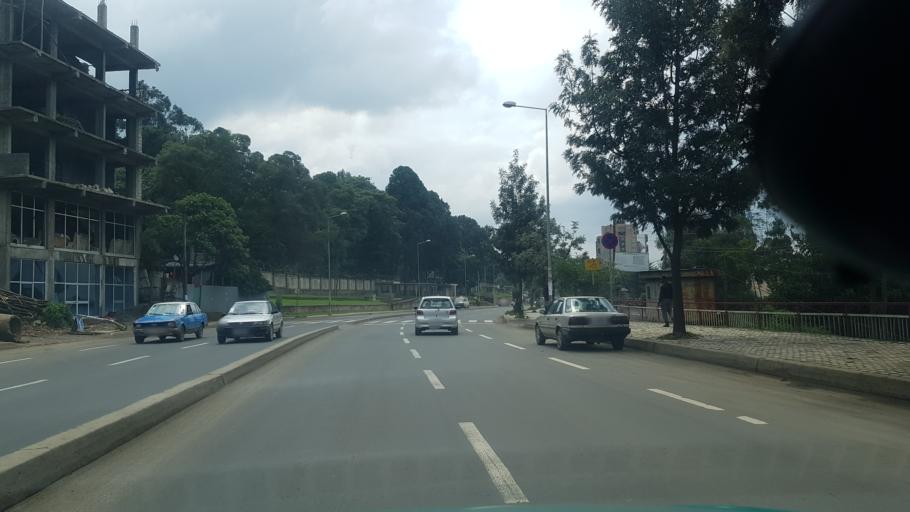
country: ET
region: Adis Abeba
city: Addis Ababa
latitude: 9.0207
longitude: 38.8046
